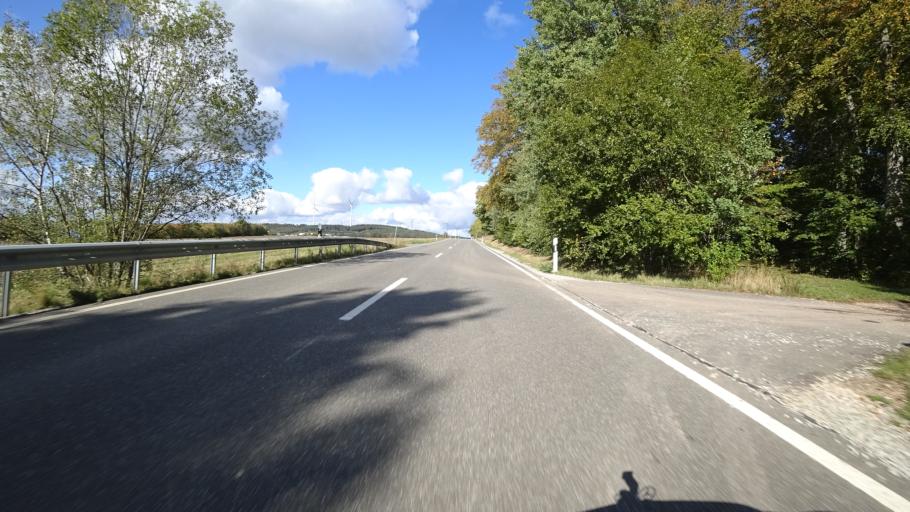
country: DE
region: Rheinland-Pfalz
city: Wiebelsheim
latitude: 50.0681
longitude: 7.6331
